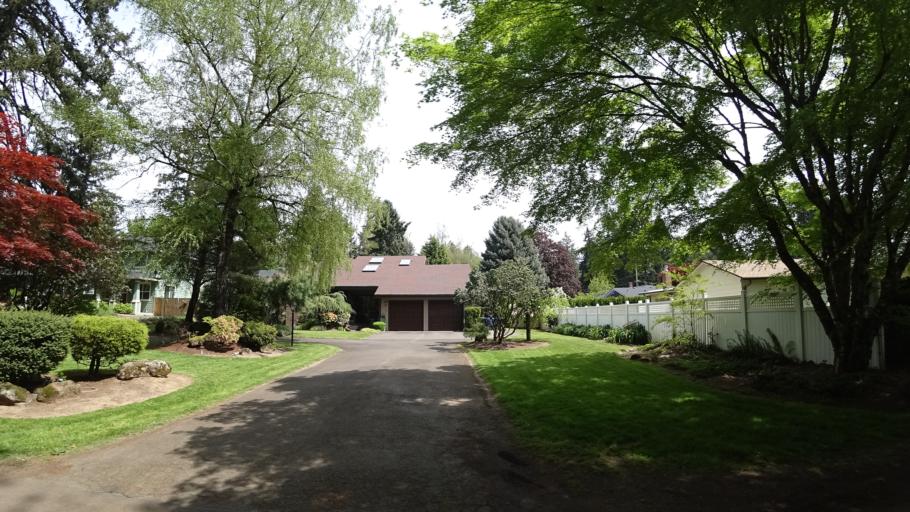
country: US
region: Oregon
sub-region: Clackamas County
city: Milwaukie
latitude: 45.4600
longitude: -122.6049
